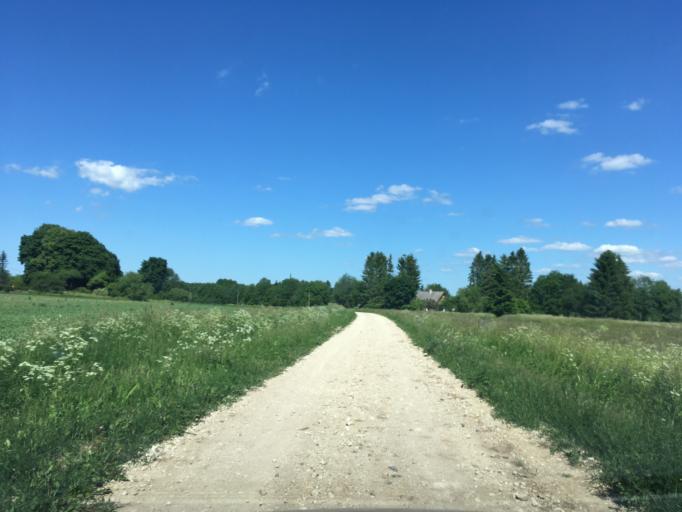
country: EE
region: Harju
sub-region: Anija vald
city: Kehra
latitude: 59.2584
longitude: 25.3018
